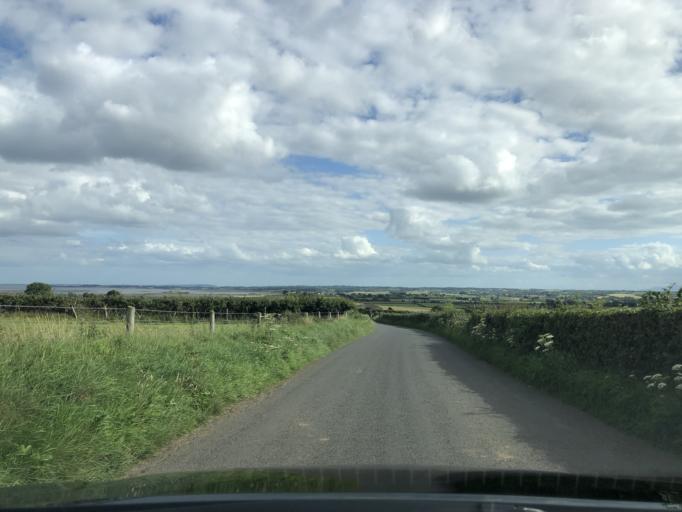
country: GB
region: Northern Ireland
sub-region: Ards District
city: Newtownards
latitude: 54.5714
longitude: -5.7138
